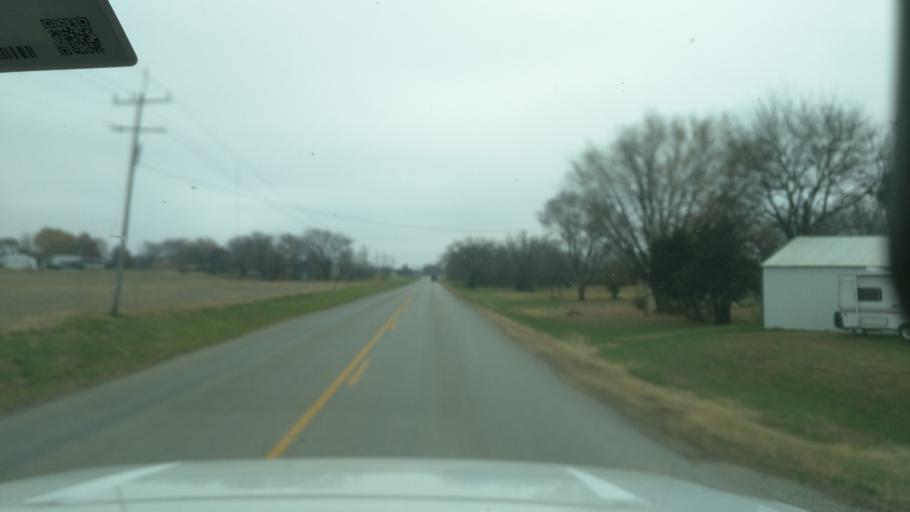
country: US
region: Kansas
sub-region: Lyon County
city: Emporia
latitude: 38.5018
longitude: -96.2588
